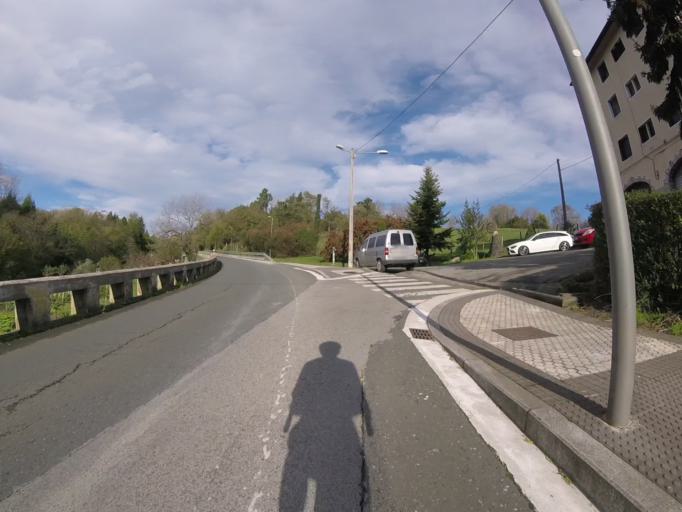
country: ES
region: Basque Country
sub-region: Provincia de Guipuzcoa
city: Hernani
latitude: 43.2746
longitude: -1.9788
